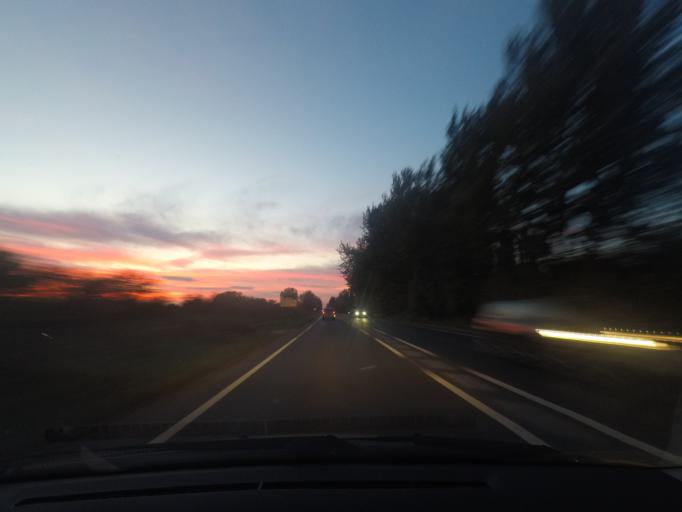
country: GB
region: England
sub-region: East Riding of Yorkshire
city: Thornton
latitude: 53.9297
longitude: -0.8228
